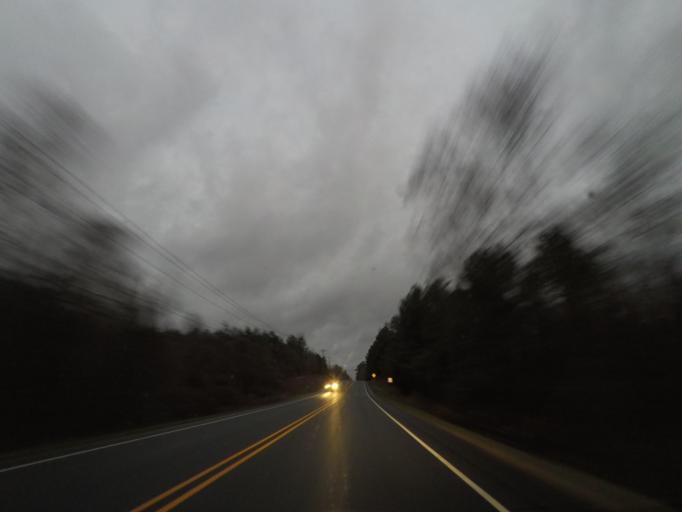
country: US
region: North Carolina
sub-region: Orange County
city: Hillsborough
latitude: 36.1065
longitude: -79.1095
